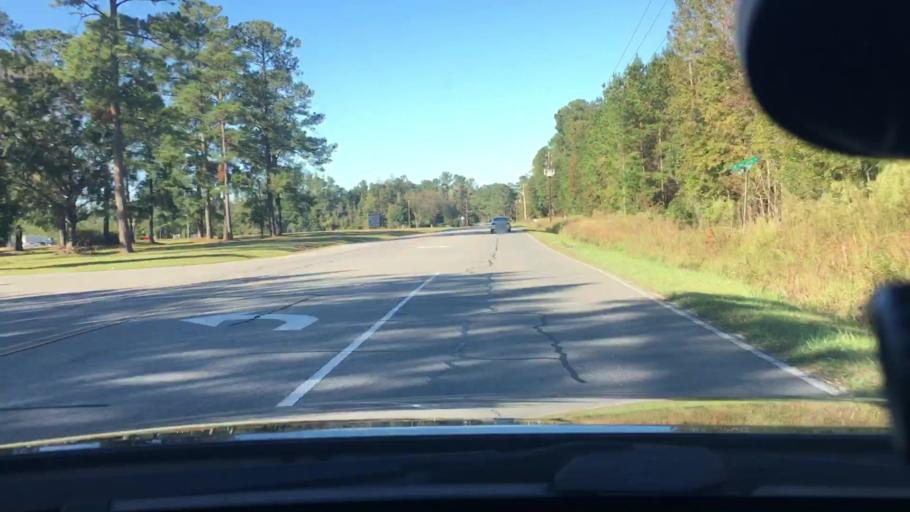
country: US
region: North Carolina
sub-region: Craven County
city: Vanceboro
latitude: 35.2355
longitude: -77.1357
